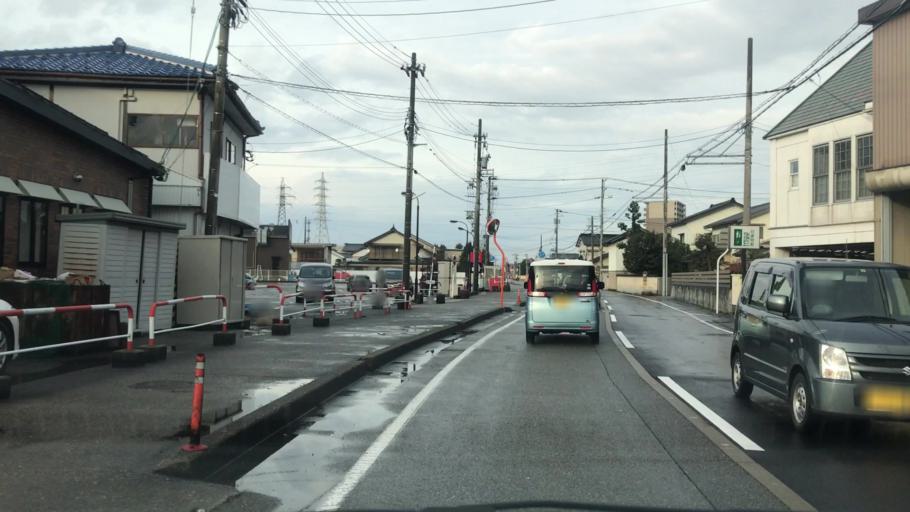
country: JP
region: Toyama
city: Toyama-shi
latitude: 36.6624
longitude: 137.2102
